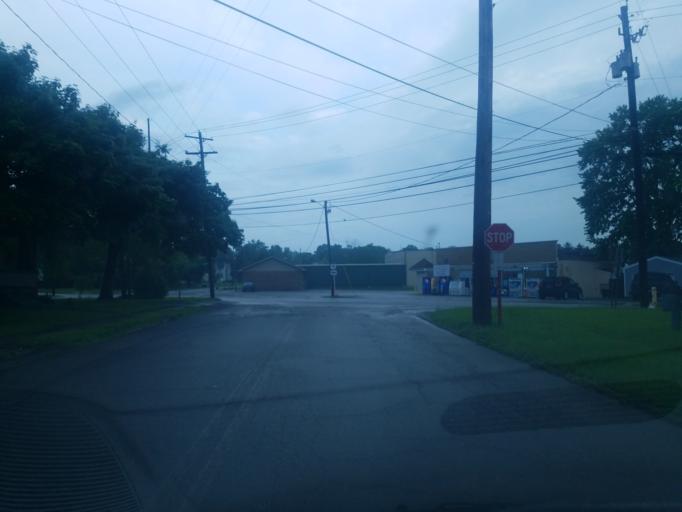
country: US
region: Ohio
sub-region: Columbiana County
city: Salem
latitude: 40.8954
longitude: -80.8617
